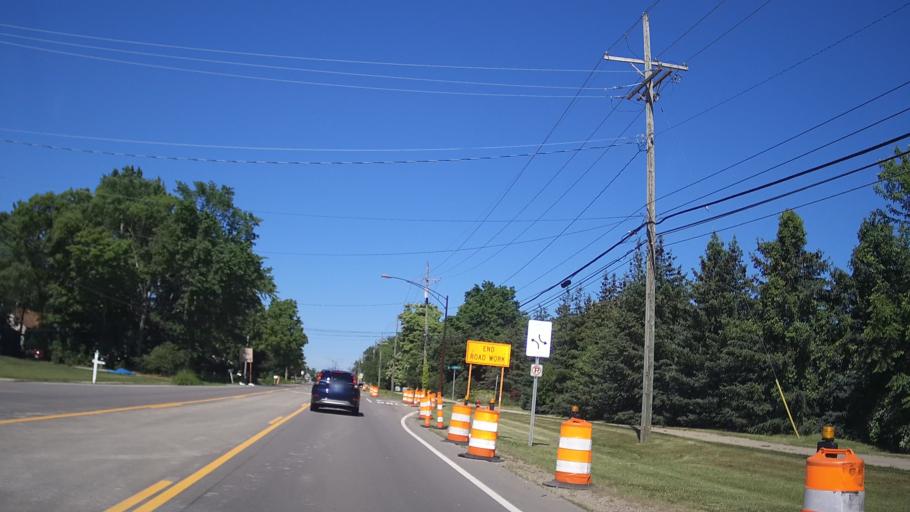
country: US
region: Michigan
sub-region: Oakland County
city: Troy
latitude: 42.6063
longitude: -83.1543
